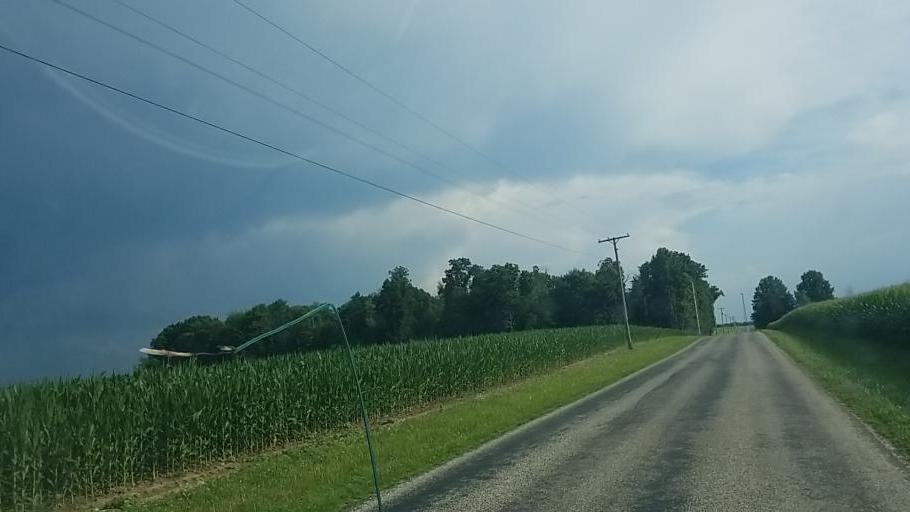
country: US
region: Ohio
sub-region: Wayne County
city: Smithville
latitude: 40.9130
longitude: -81.8593
